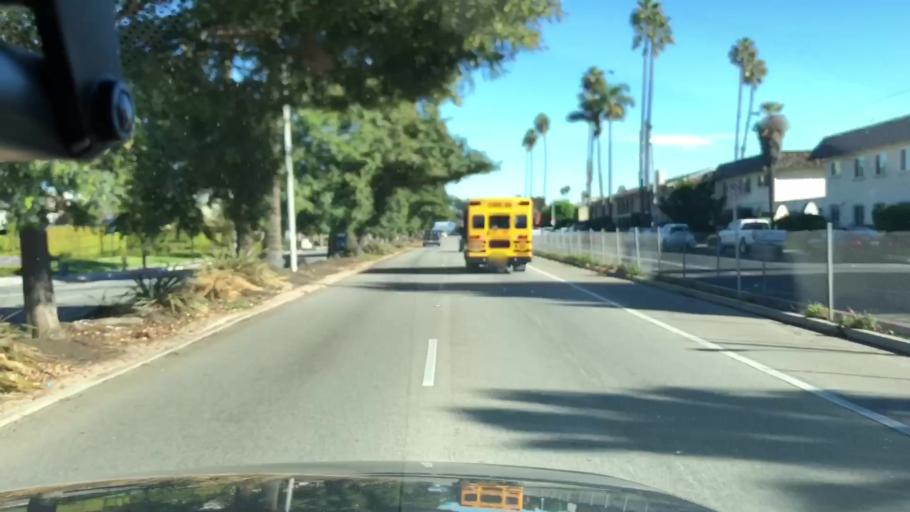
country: US
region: California
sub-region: Ventura County
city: Oxnard
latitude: 34.2191
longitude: -119.1845
